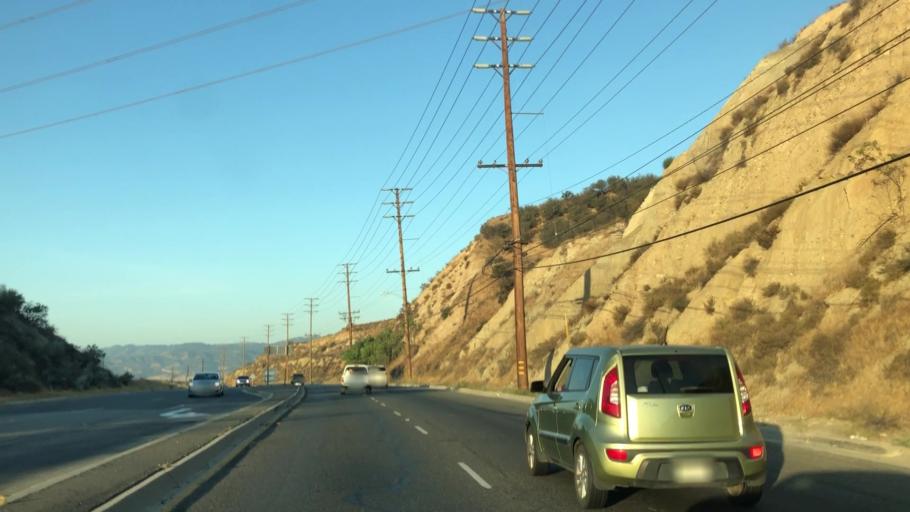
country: US
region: California
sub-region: Los Angeles County
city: Santa Clarita
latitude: 34.3948
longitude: -118.4859
